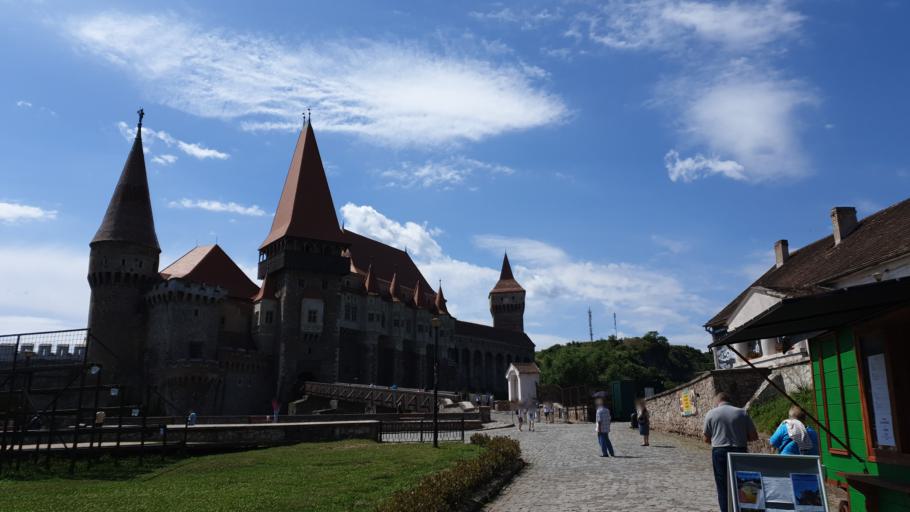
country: RO
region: Hunedoara
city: Hunedoara
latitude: 45.7506
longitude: 22.8882
